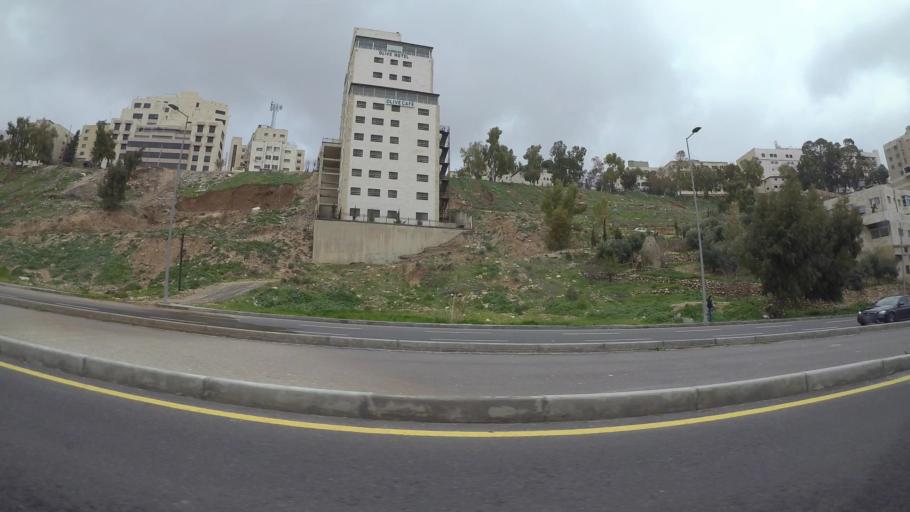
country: JO
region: Amman
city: Amman
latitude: 31.9502
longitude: 35.9016
